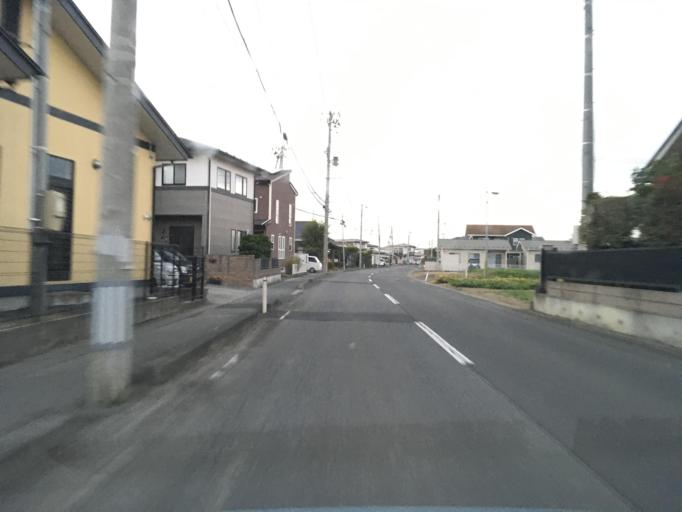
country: JP
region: Miyagi
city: Wakuya
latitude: 38.7039
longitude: 141.2168
